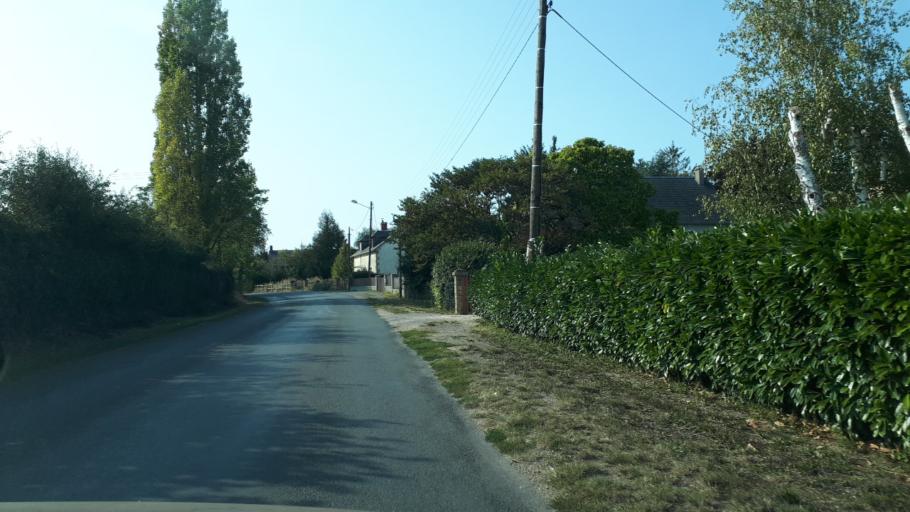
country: FR
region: Centre
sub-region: Departement du Cher
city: Rians
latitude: 47.1842
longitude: 2.7059
